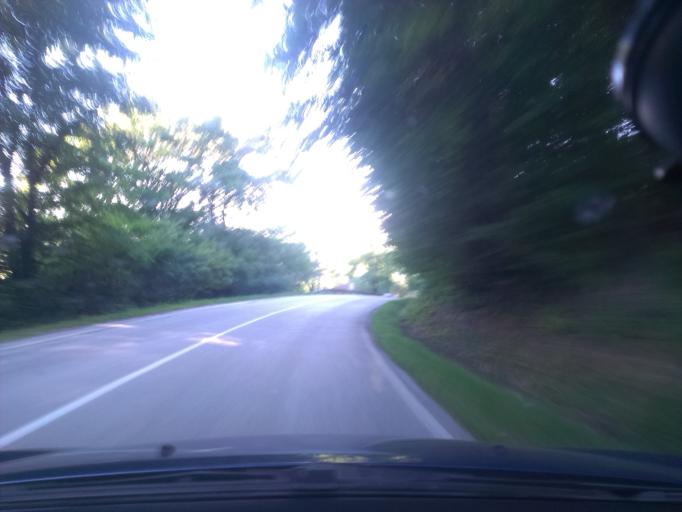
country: SK
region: Trenciansky
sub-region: Okres Myjava
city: Myjava
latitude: 48.8101
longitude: 17.5217
